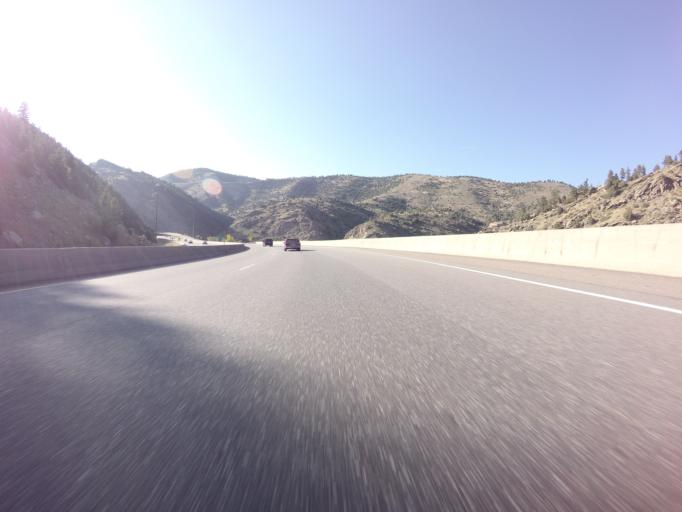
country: US
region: Colorado
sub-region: Clear Creek County
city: Idaho Springs
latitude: 39.7432
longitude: -105.4335
